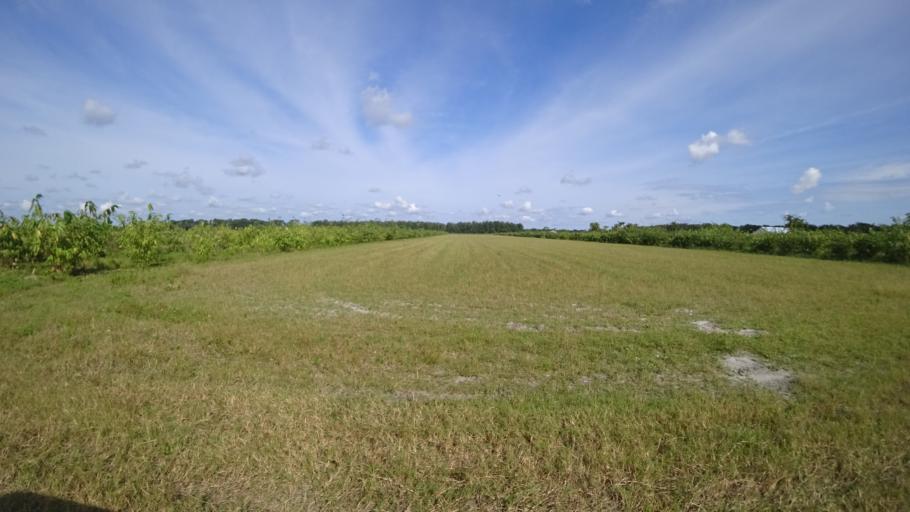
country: US
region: Florida
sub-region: Sarasota County
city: The Meadows
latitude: 27.4438
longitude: -82.3099
